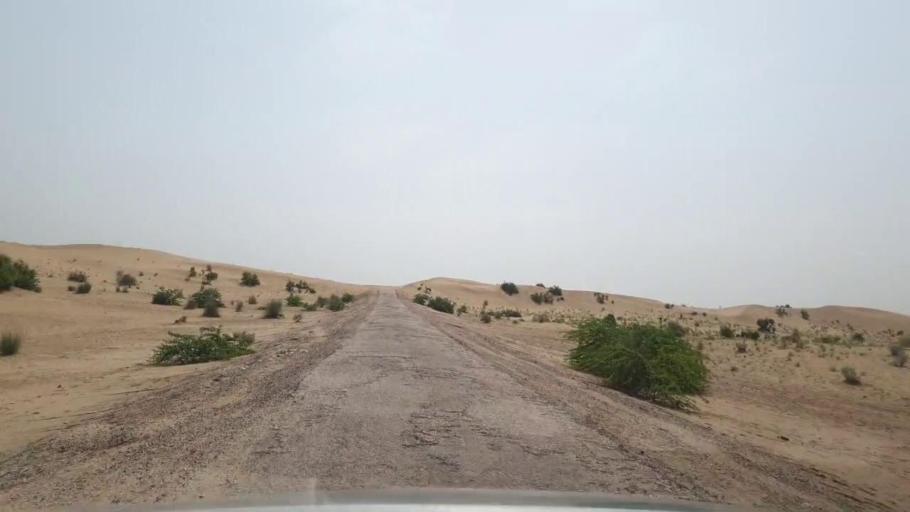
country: PK
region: Sindh
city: Rohri
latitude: 27.6178
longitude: 69.1154
